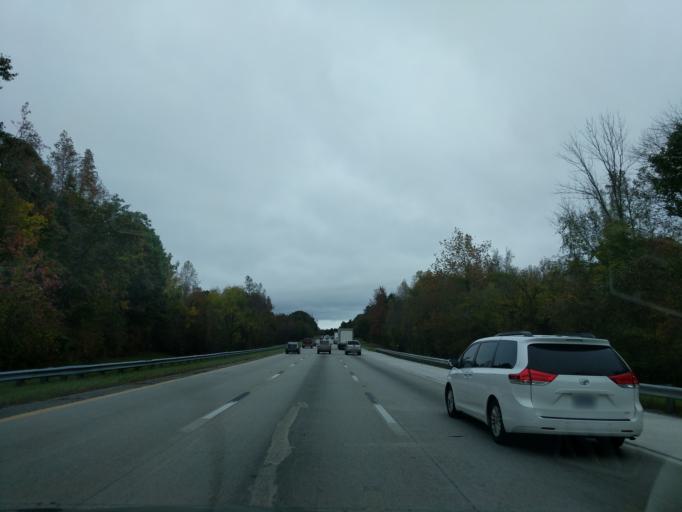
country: US
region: North Carolina
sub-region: Guilford County
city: Jamestown
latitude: 35.9705
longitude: -79.8912
